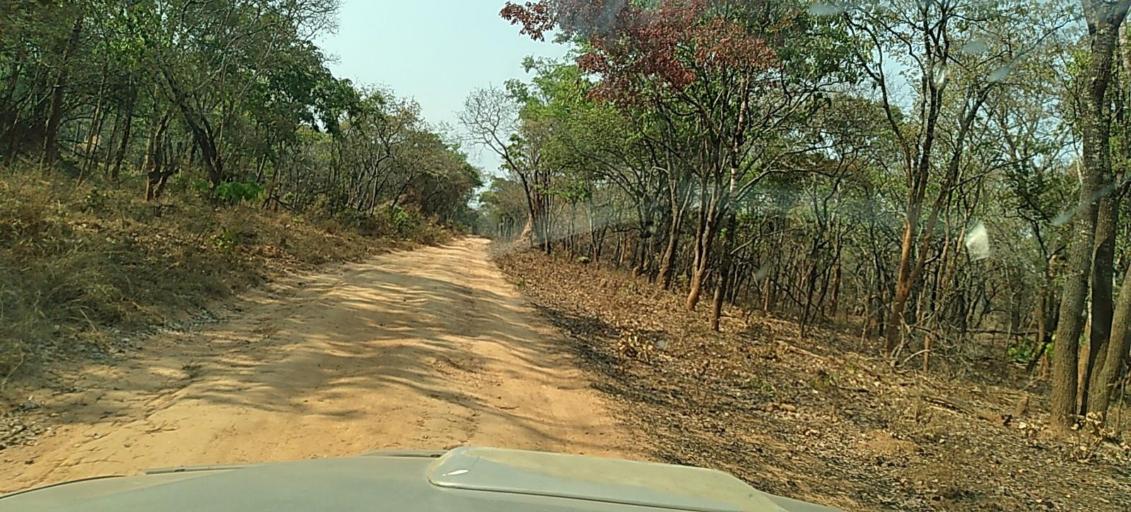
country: ZM
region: North-Western
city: Kasempa
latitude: -13.5290
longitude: 26.4092
